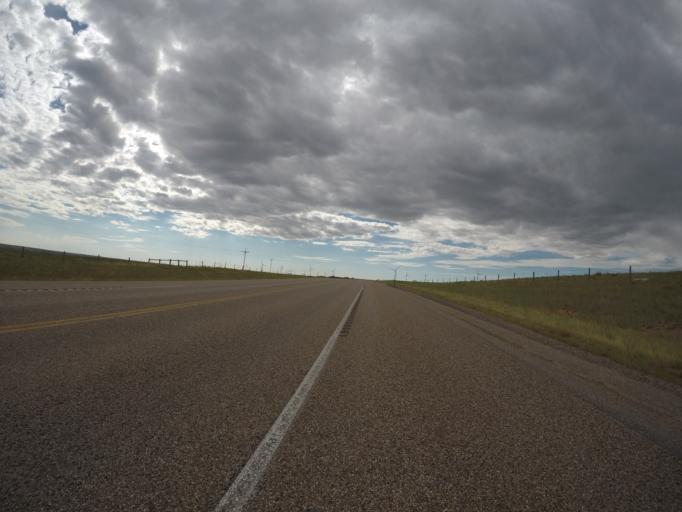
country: US
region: Wyoming
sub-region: Laramie County
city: Cheyenne
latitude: 41.1531
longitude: -105.0345
